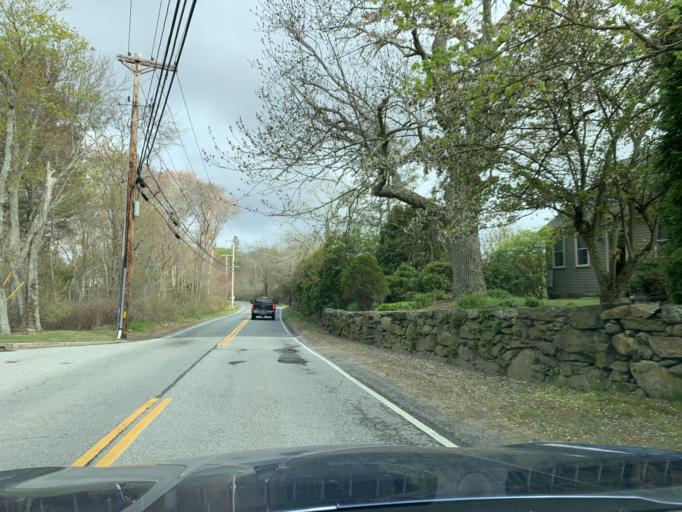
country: US
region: Rhode Island
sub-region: Washington County
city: North Kingstown
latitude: 41.5918
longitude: -71.4843
